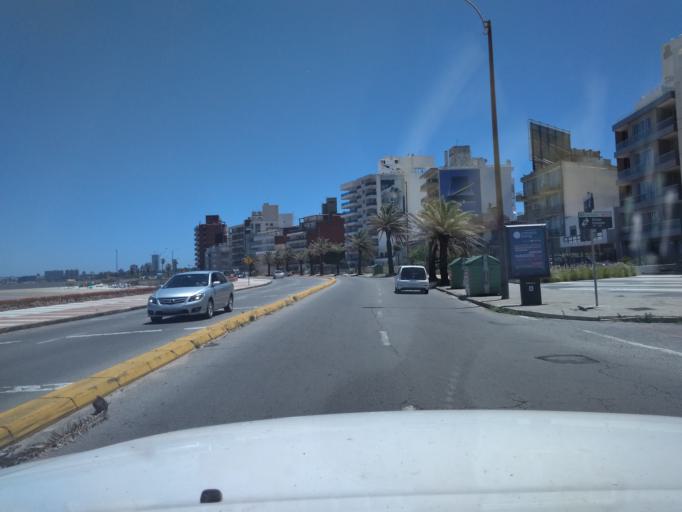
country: UY
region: Canelones
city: Paso de Carrasco
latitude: -34.8967
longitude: -56.0971
